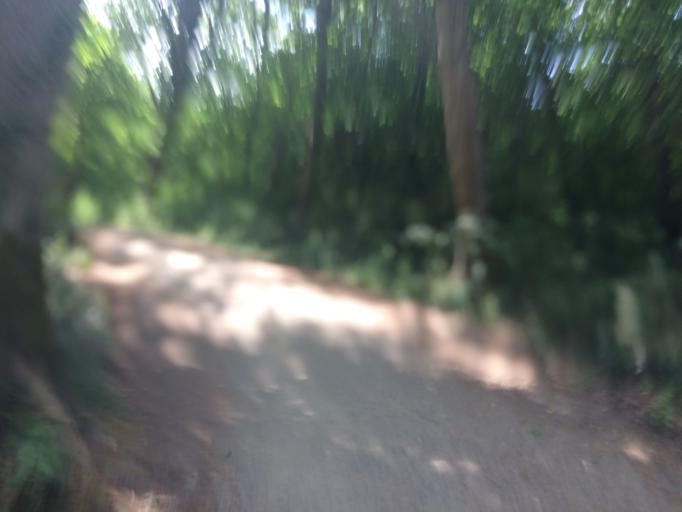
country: DK
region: Capital Region
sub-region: Bornholm Kommune
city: Ronne
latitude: 55.1239
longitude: 14.7076
